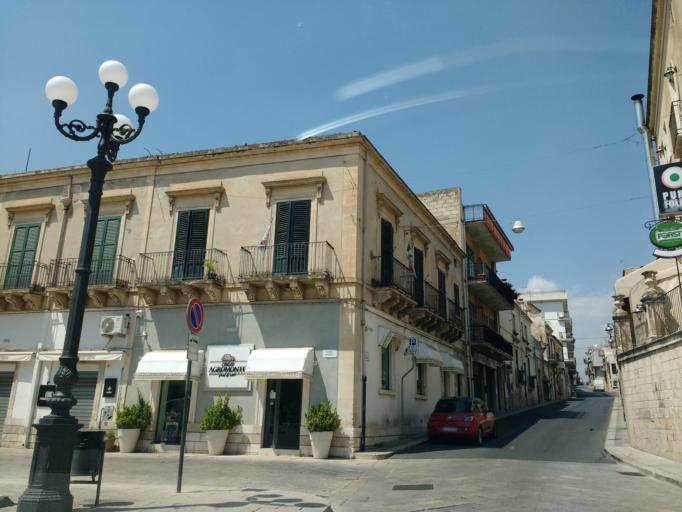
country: IT
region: Sicily
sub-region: Ragusa
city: Scicli
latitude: 36.7951
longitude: 14.7071
